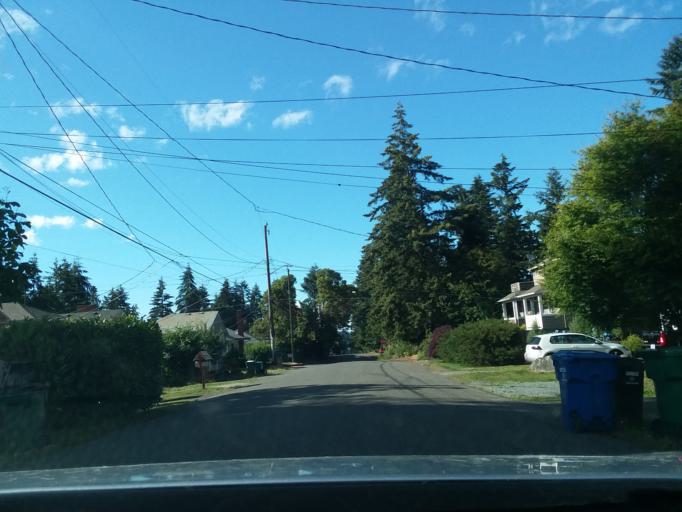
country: US
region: Washington
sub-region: King County
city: Shoreline
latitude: 47.7333
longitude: -122.3370
